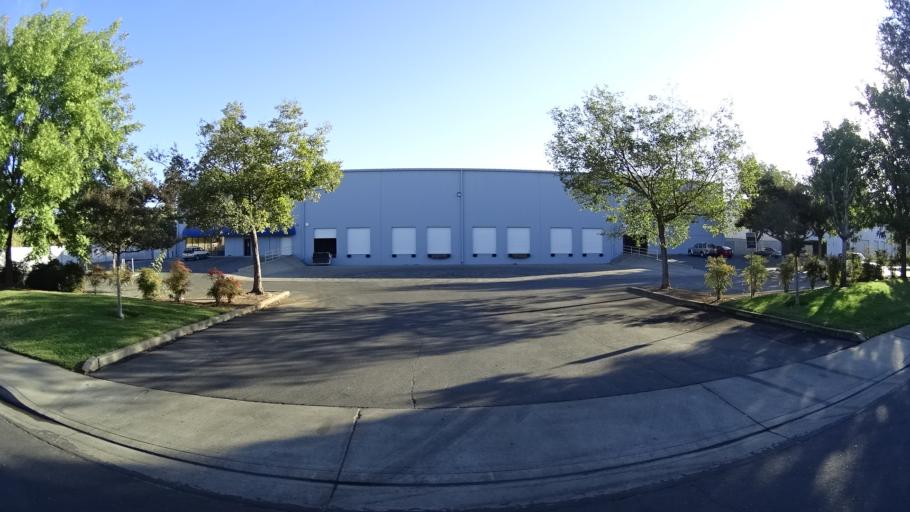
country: US
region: California
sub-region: Sacramento County
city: Florin
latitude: 38.5178
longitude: -121.3802
